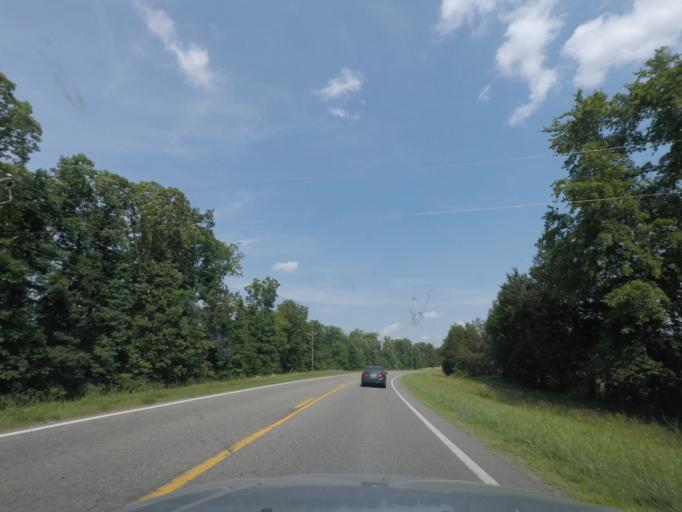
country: US
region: Virginia
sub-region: Fluvanna County
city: Palmyra
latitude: 37.8150
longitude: -78.2500
